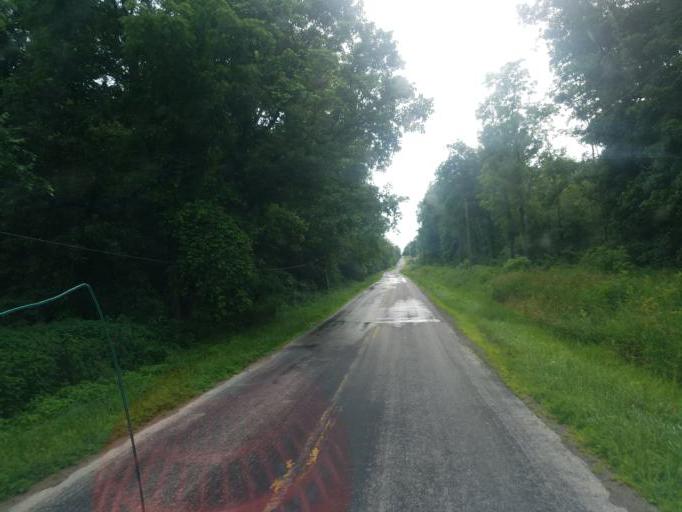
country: US
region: Ohio
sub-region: Wayne County
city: West Salem
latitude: 40.9009
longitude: -82.1360
